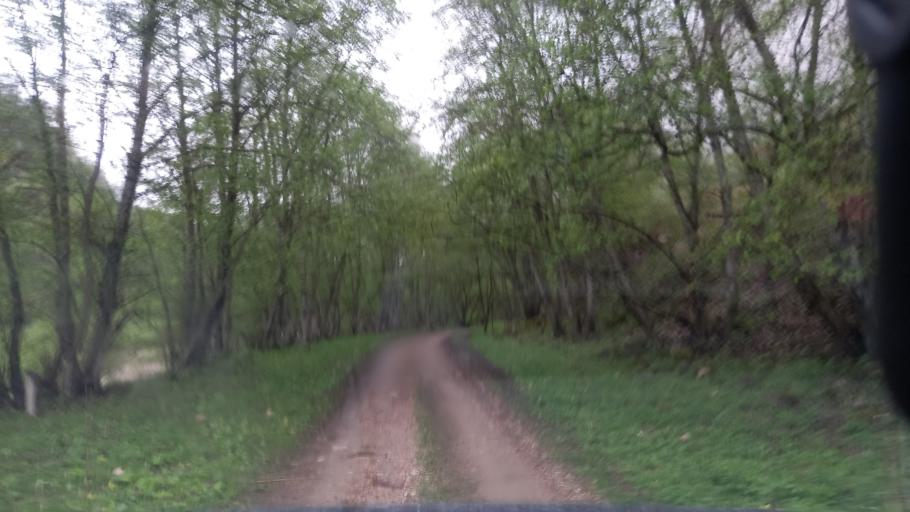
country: RU
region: Kabardino-Balkariya
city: Bylym
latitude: 43.5950
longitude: 42.9619
